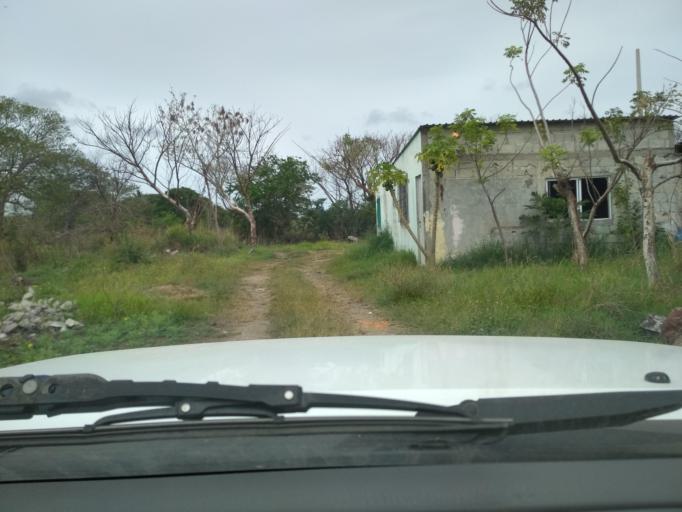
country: MX
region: Veracruz
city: El Tejar
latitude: 19.0647
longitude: -96.1389
